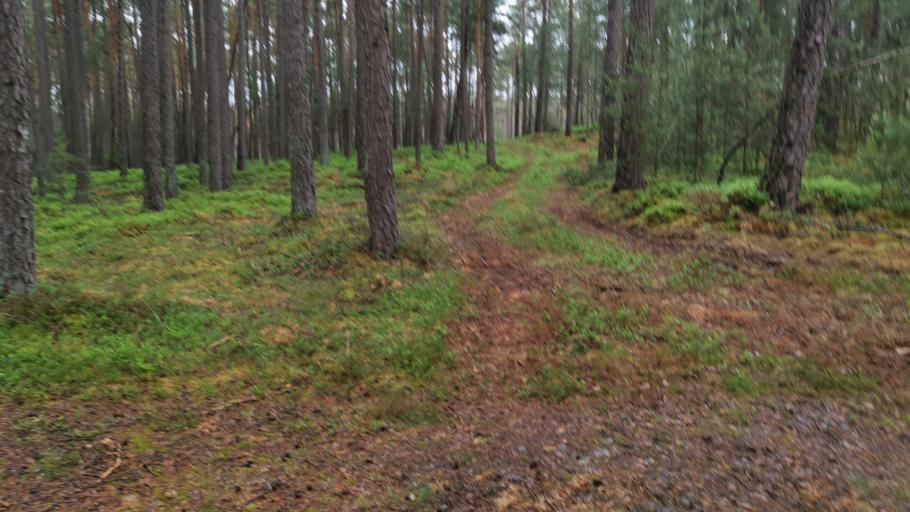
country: DE
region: Bavaria
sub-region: Regierungsbezirk Mittelfranken
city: Roth
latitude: 49.2569
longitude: 11.1157
